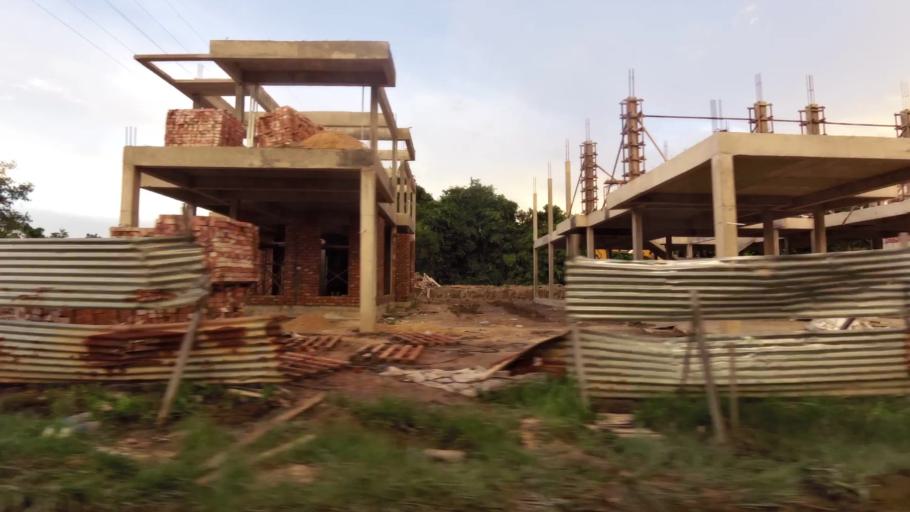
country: BN
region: Brunei and Muara
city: Bandar Seri Begawan
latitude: 4.9970
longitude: 115.0012
